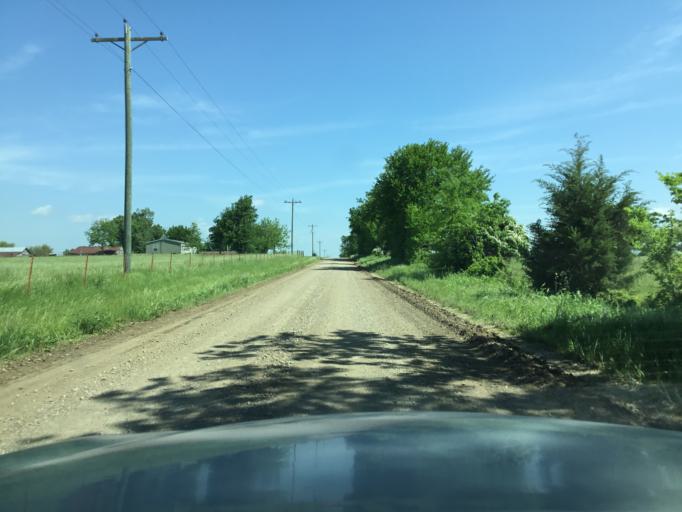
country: US
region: Kansas
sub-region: Labette County
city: Oswego
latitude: 37.1732
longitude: -95.1399
